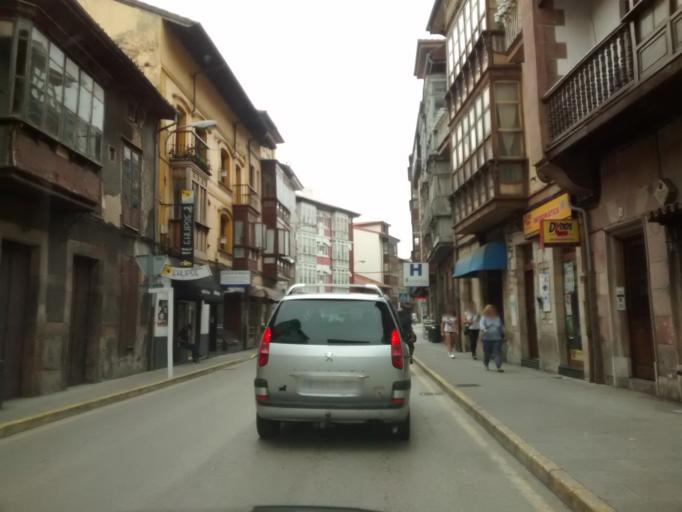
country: ES
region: Cantabria
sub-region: Provincia de Cantabria
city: Cabezon de la Sal
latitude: 43.3084
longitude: -4.2375
